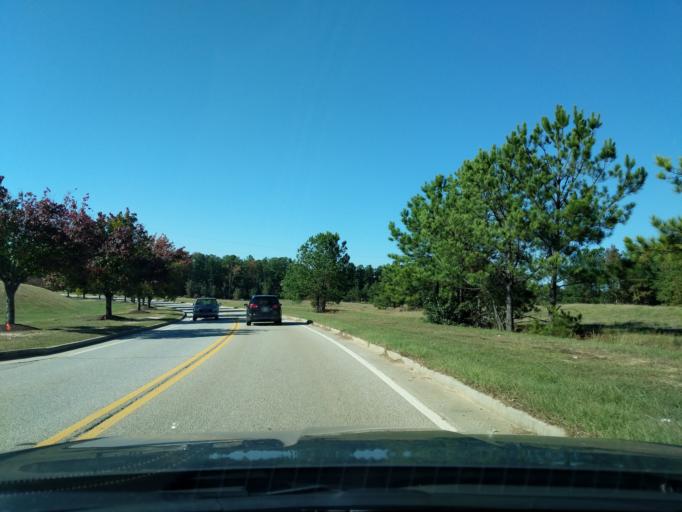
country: US
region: Georgia
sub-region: Columbia County
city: Grovetown
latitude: 33.4650
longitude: -82.1834
